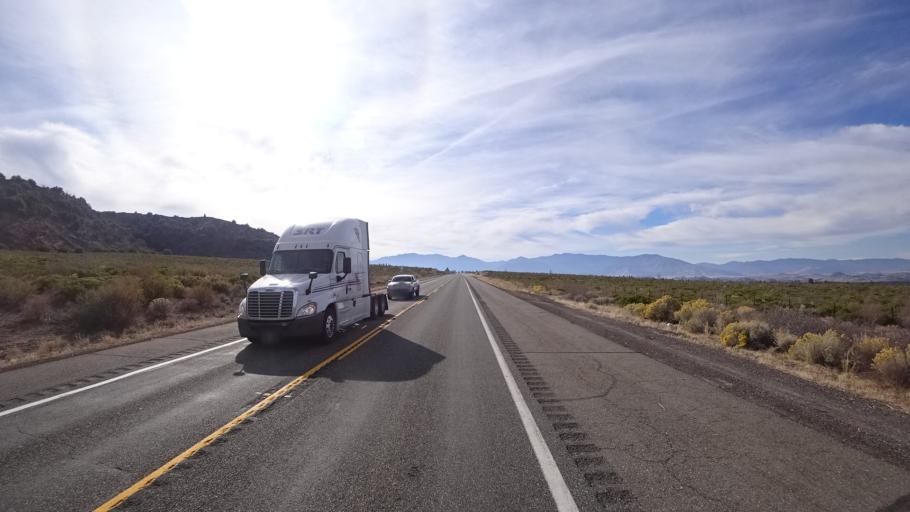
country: US
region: California
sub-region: Siskiyou County
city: Weed
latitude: 41.5154
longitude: -122.3107
